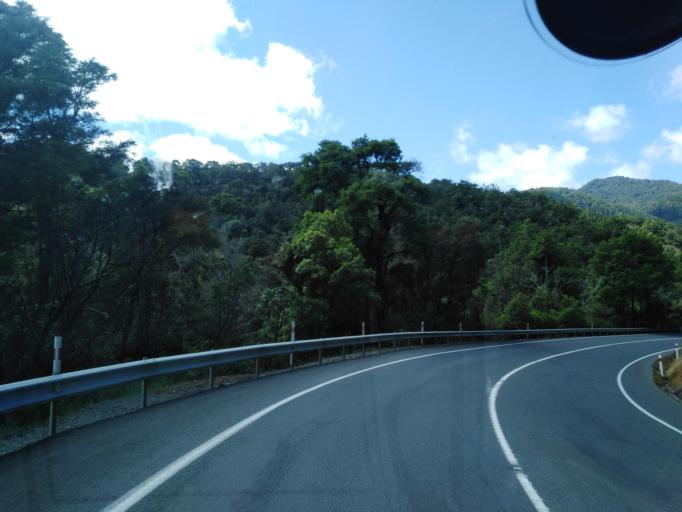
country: NZ
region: Nelson
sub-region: Nelson City
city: Nelson
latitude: -41.2246
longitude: 173.4357
